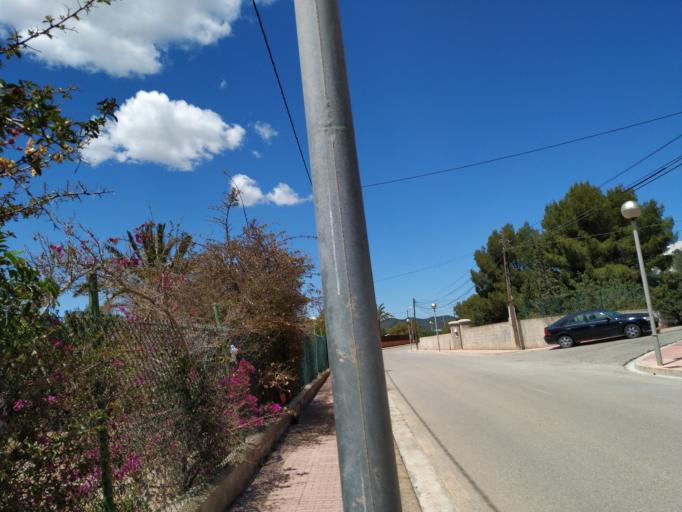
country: ES
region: Balearic Islands
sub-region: Illes Balears
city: Ibiza
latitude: 38.9164
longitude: 1.4724
